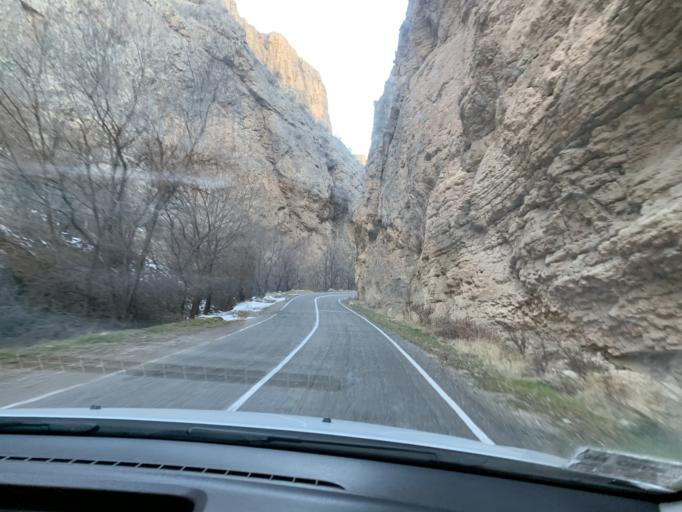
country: AM
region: Vayots' Dzori Marz
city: Areni
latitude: 39.7201
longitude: 45.2044
